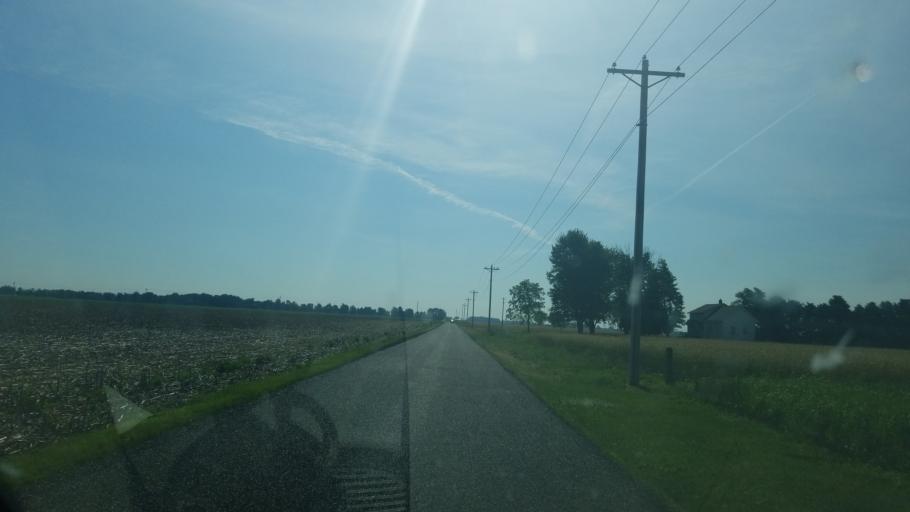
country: US
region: Ohio
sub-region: Hancock County
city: Findlay
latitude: 41.0214
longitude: -83.5502
